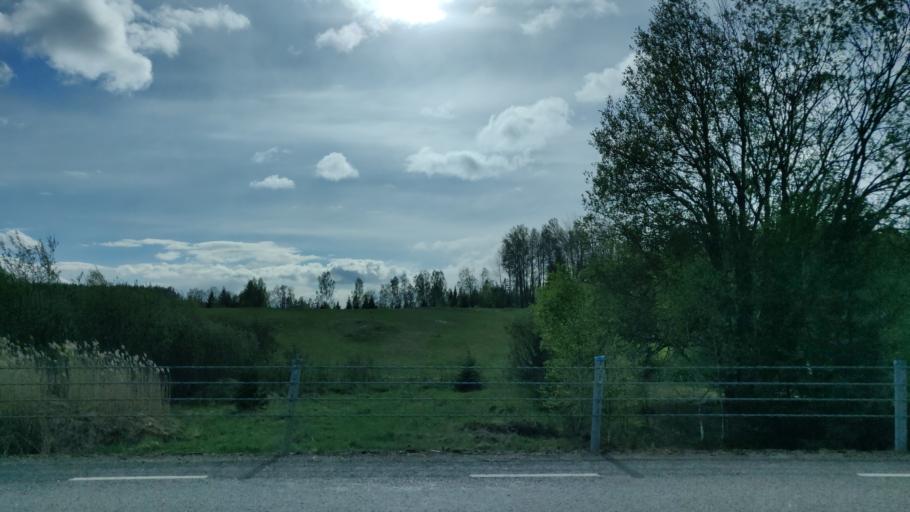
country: SE
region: Vaermland
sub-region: Forshaga Kommun
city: Deje
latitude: 59.5773
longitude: 13.4692
